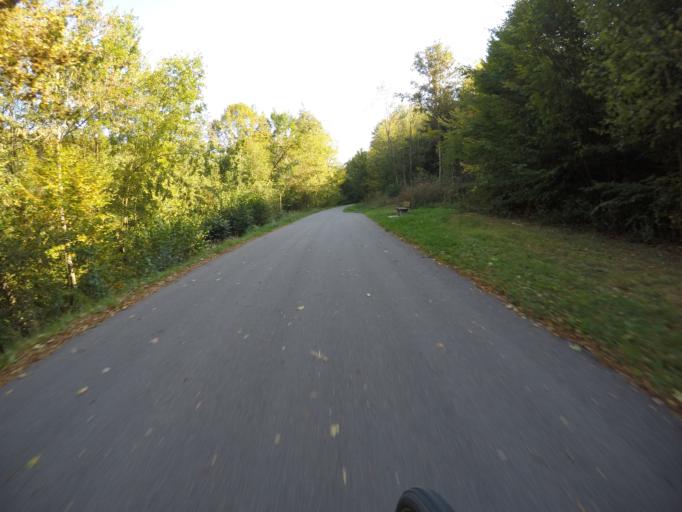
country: DE
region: Baden-Wuerttemberg
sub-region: Regierungsbezirk Stuttgart
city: Waldenbuch
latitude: 48.6383
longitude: 9.1694
